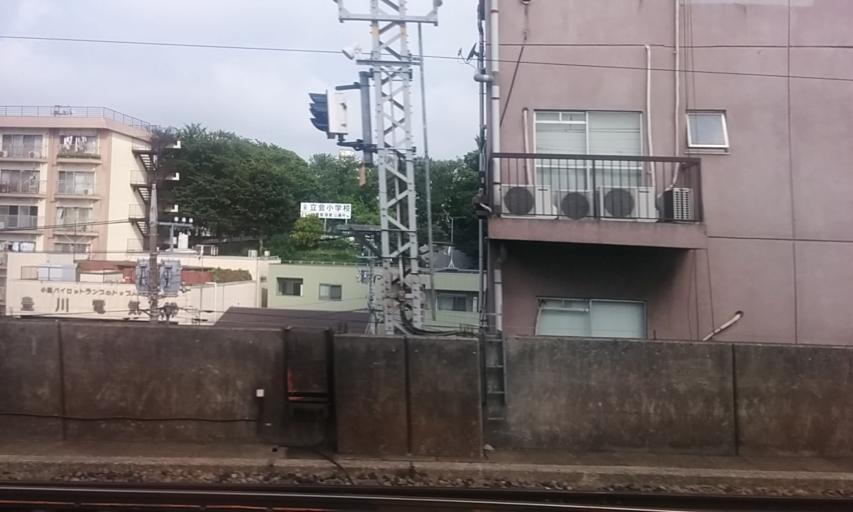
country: JP
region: Kanagawa
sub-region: Kawasaki-shi
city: Kawasaki
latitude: 35.6042
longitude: 139.7417
